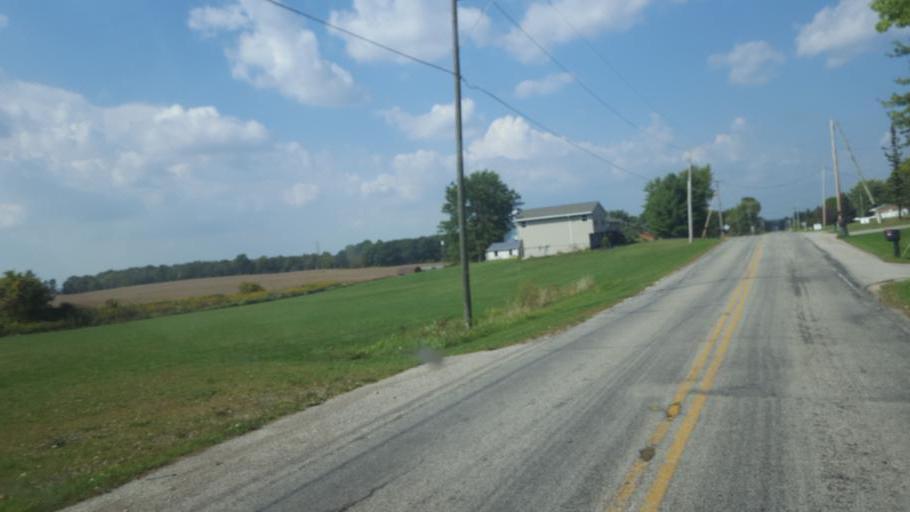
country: US
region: Ohio
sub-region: Richland County
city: Ontario
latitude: 40.7984
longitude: -82.6285
